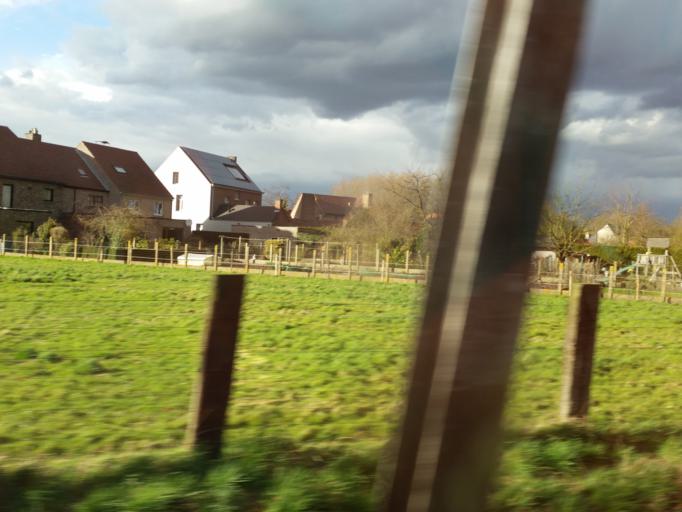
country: BE
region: Flanders
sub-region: Provincie Oost-Vlaanderen
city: Dendermonde
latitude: 51.0206
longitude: 4.0891
